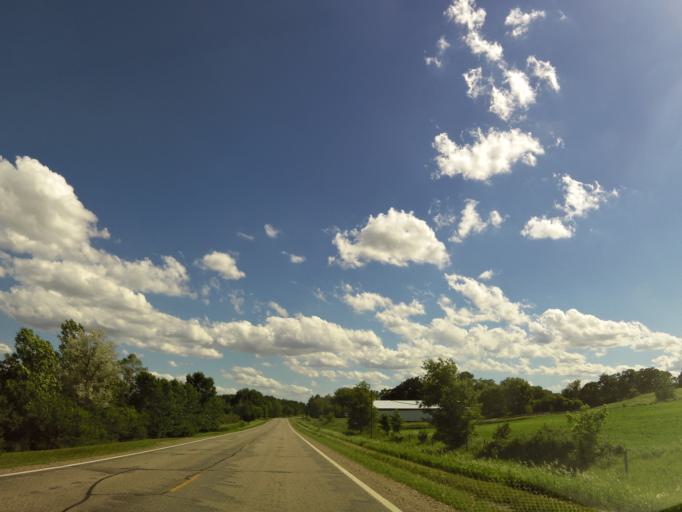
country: US
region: Minnesota
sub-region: Meeker County
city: Dassel
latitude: 45.1130
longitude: -94.3007
